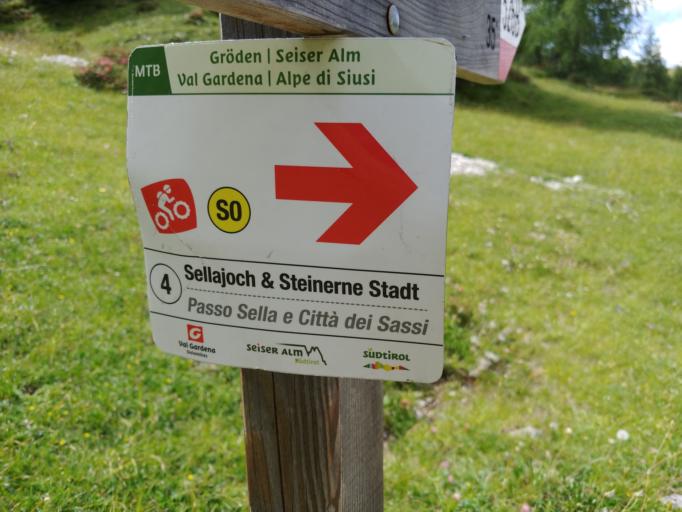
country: IT
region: Trentino-Alto Adige
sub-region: Bolzano
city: Santa Cristina Valgardena
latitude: 46.5327
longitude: 11.7370
